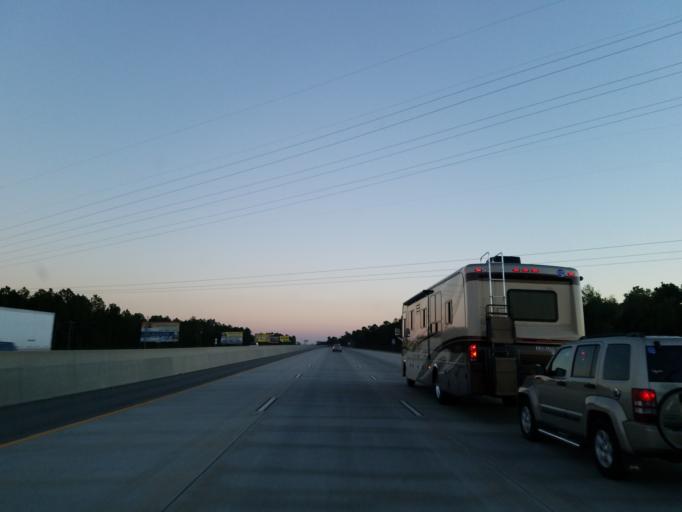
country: US
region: Georgia
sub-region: Cook County
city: Sparks
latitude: 31.2111
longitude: -83.4595
